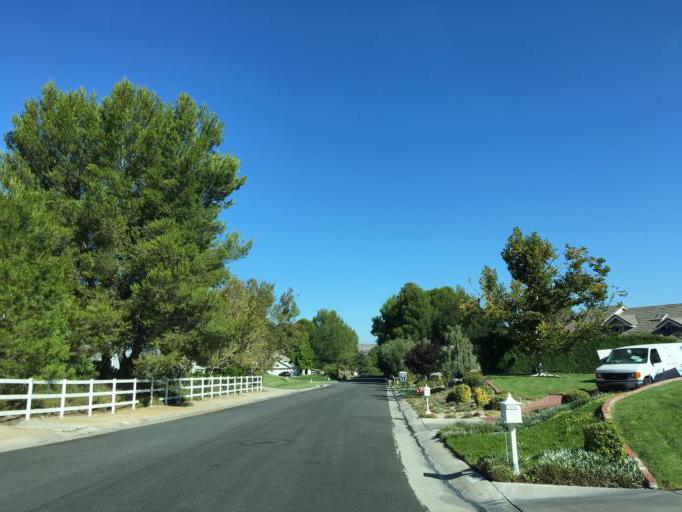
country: US
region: California
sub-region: Los Angeles County
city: San Fernando
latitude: 34.3996
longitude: -118.4065
